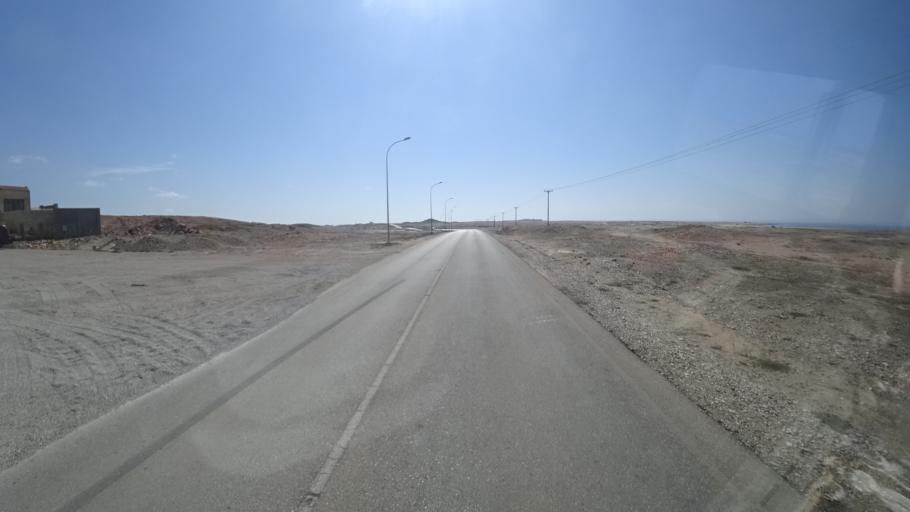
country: OM
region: Zufar
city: Salalah
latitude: 16.9734
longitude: 54.7176
